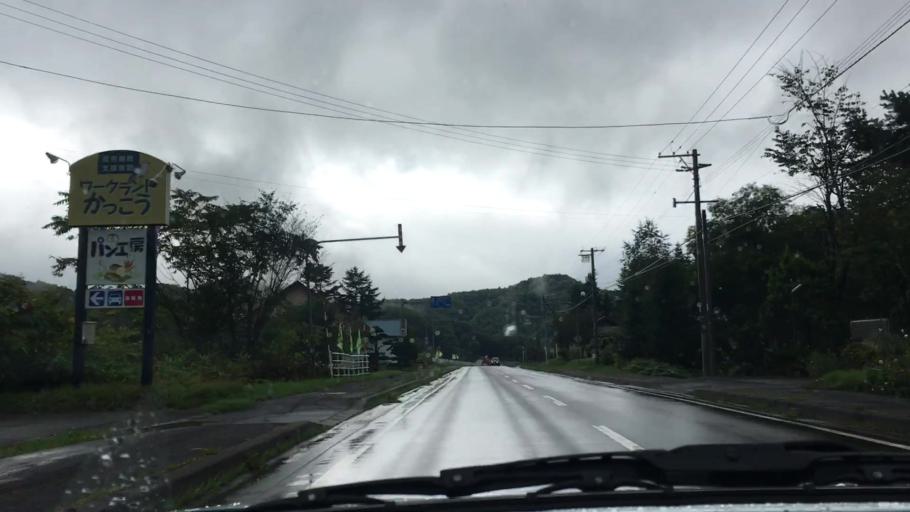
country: JP
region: Hokkaido
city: Niseko Town
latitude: 42.6437
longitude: 140.7330
